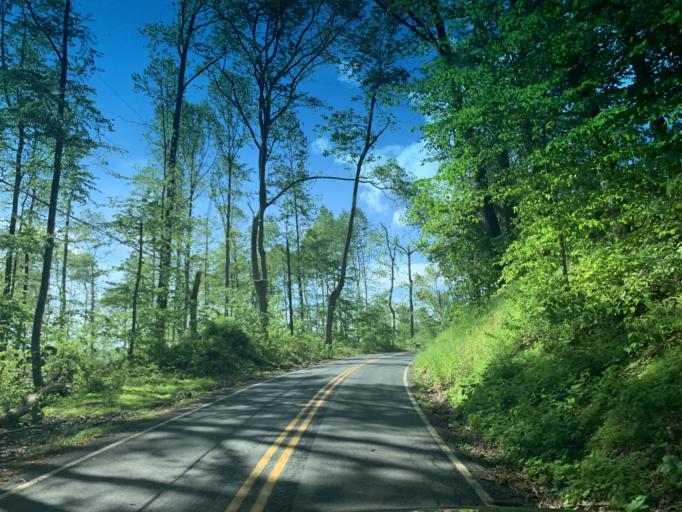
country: US
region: Maryland
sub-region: Cecil County
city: Rising Sun
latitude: 39.6912
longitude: -76.1864
